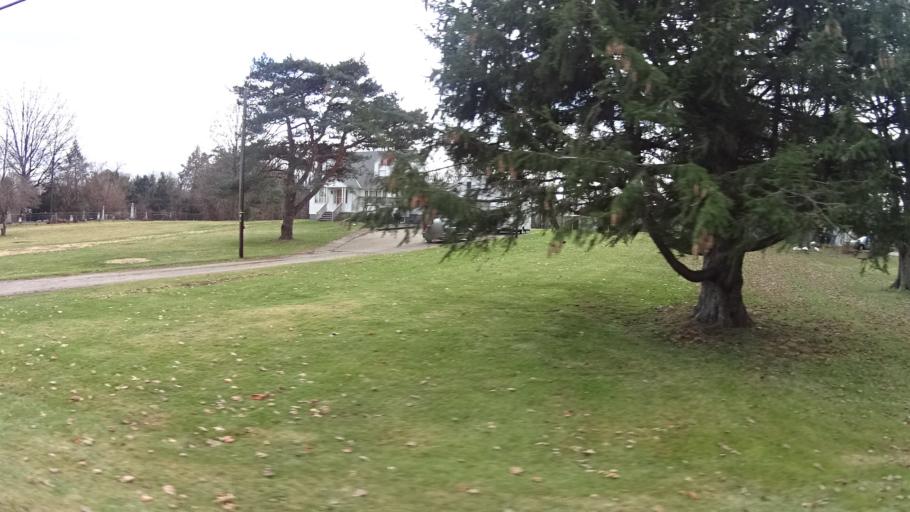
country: US
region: Ohio
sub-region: Lorain County
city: North Ridgeville
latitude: 41.3676
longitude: -82.0536
